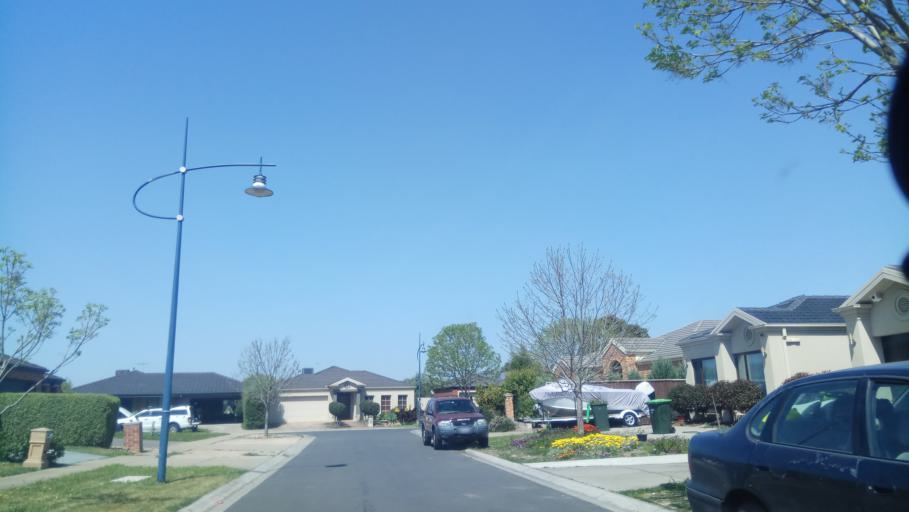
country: AU
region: Victoria
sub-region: Wyndham
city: Point Cook
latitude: -37.8916
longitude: 144.7415
